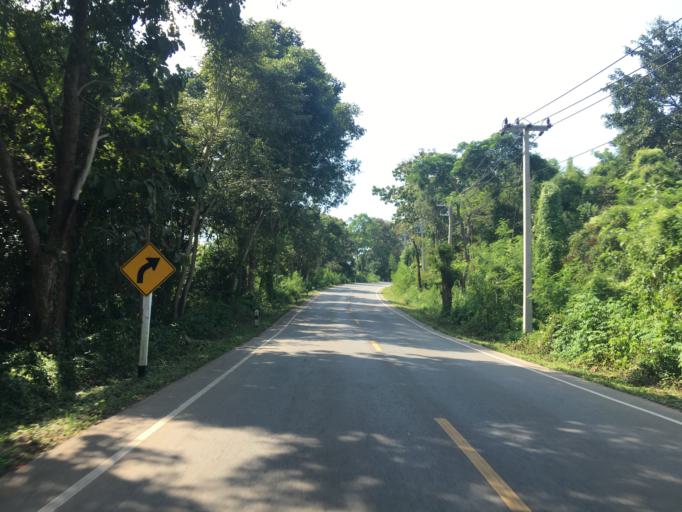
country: TH
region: Nan
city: Ban Luang
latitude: 18.8430
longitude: 100.4164
